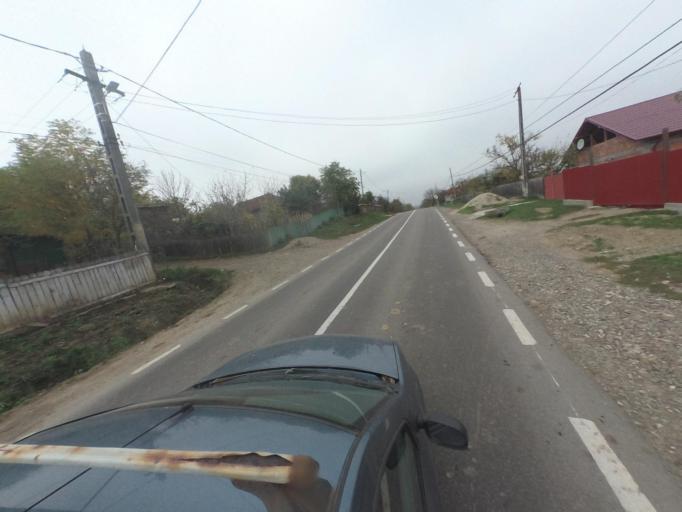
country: RO
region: Vaslui
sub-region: Comuna Bacesti
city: Bacesti
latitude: 46.8307
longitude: 27.2368
